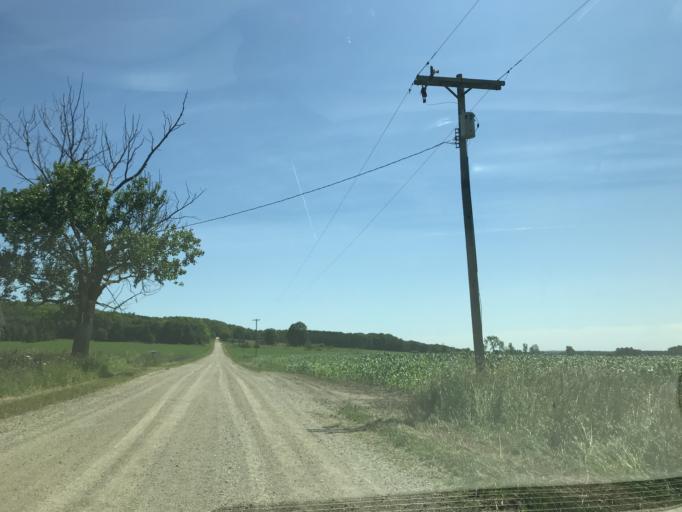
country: US
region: Michigan
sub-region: Missaukee County
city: Lake City
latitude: 44.2791
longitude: -85.0492
